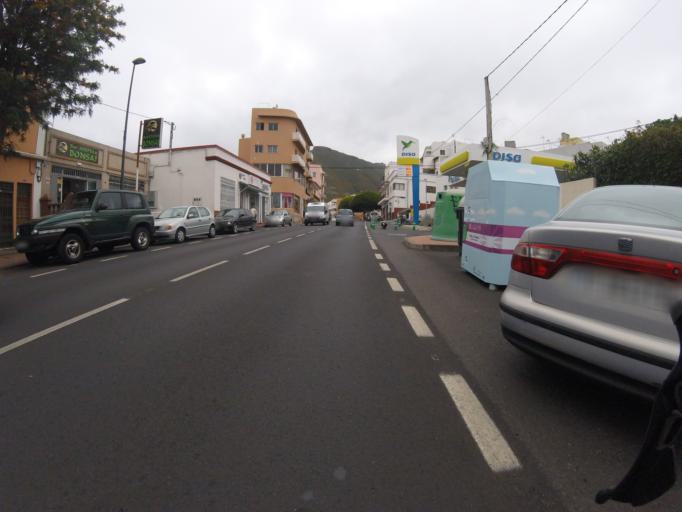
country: ES
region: Canary Islands
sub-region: Provincia de Santa Cruz de Tenerife
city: Tegueste
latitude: 28.5338
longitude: -16.3635
